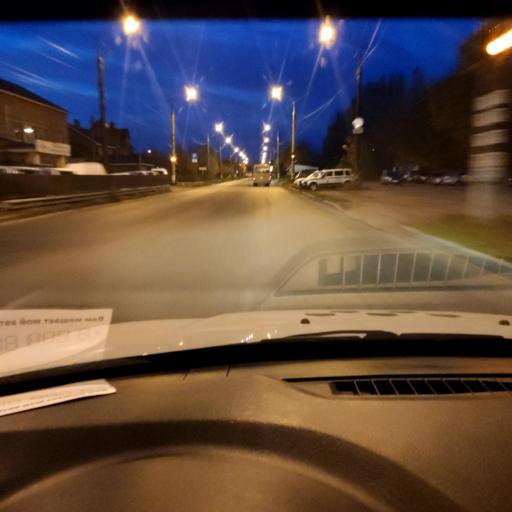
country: RU
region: Samara
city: Tol'yatti
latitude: 53.5138
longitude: 49.3954
